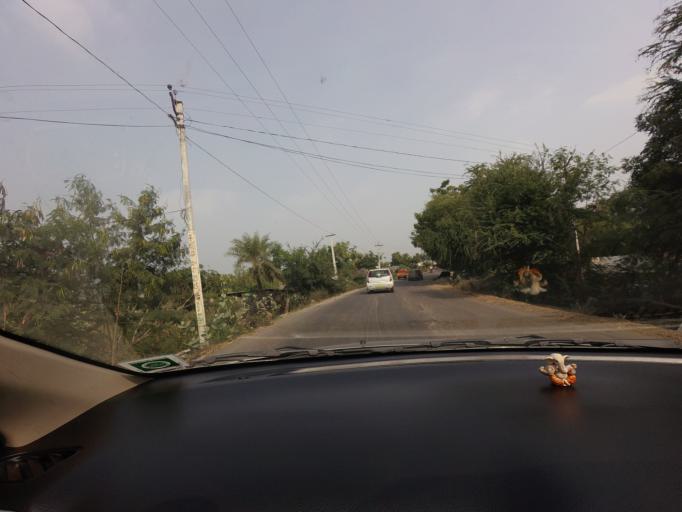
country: IN
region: Andhra Pradesh
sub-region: Krishna
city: Kankipadu
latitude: 16.4562
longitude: 80.7958
